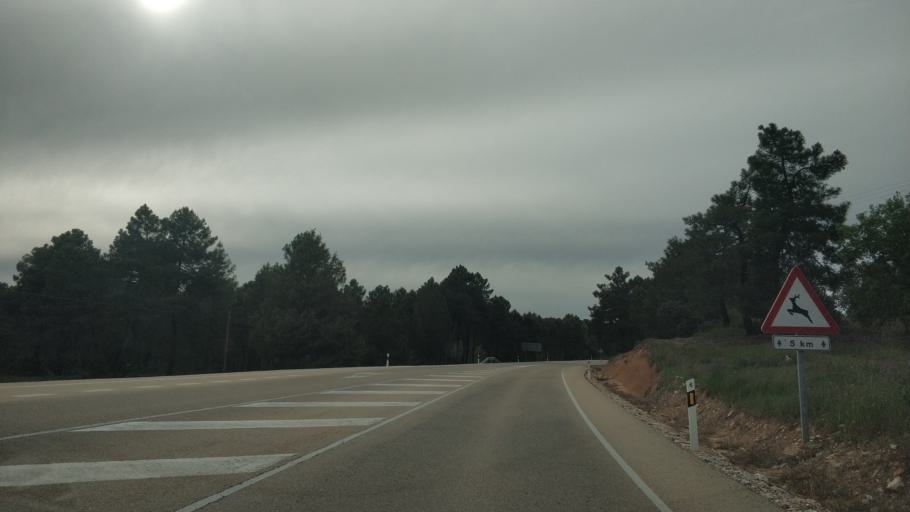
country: ES
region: Castille and Leon
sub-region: Provincia de Soria
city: Bayubas de Abajo
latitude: 41.5121
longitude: -2.9249
